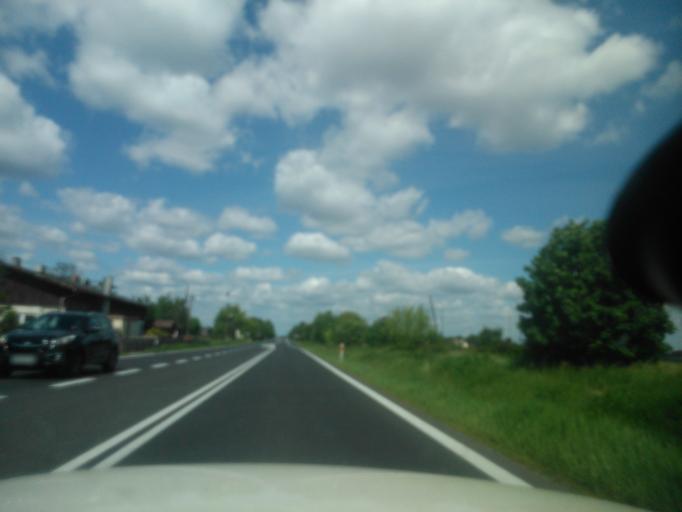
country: PL
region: Kujawsko-Pomorskie
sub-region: Powiat torunski
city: Lubicz Gorny
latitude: 53.0109
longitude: 18.8282
